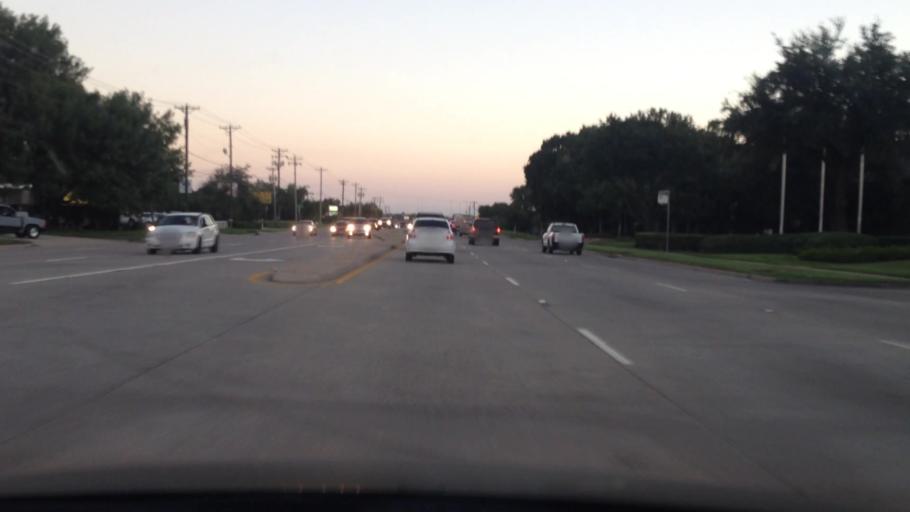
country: US
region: Texas
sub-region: Denton County
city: Lewisville
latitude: 33.0246
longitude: -96.9930
